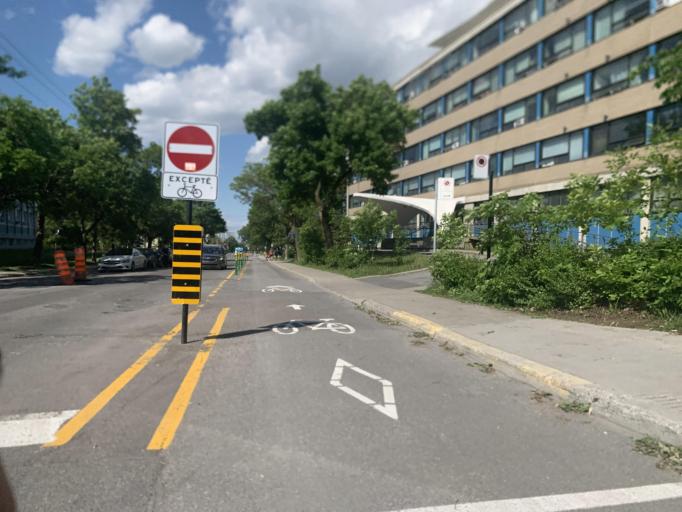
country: CA
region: Quebec
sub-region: Montreal
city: Saint-Leonard
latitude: 45.5600
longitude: -73.5771
